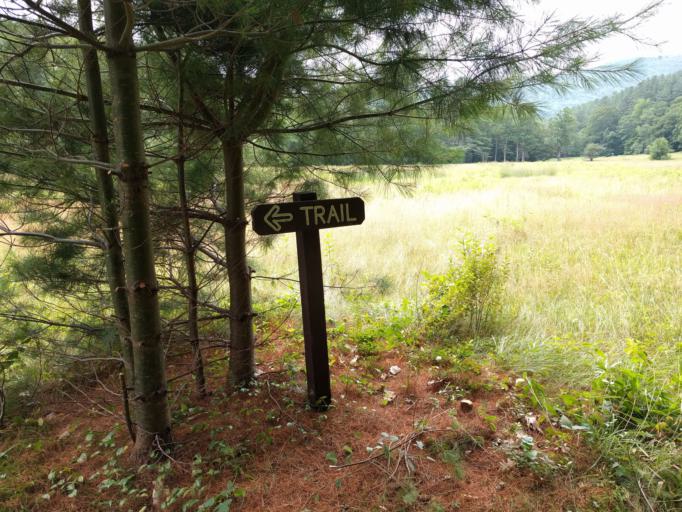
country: US
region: Massachusetts
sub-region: Franklin County
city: Charlemont
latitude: 42.6470
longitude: -72.9318
